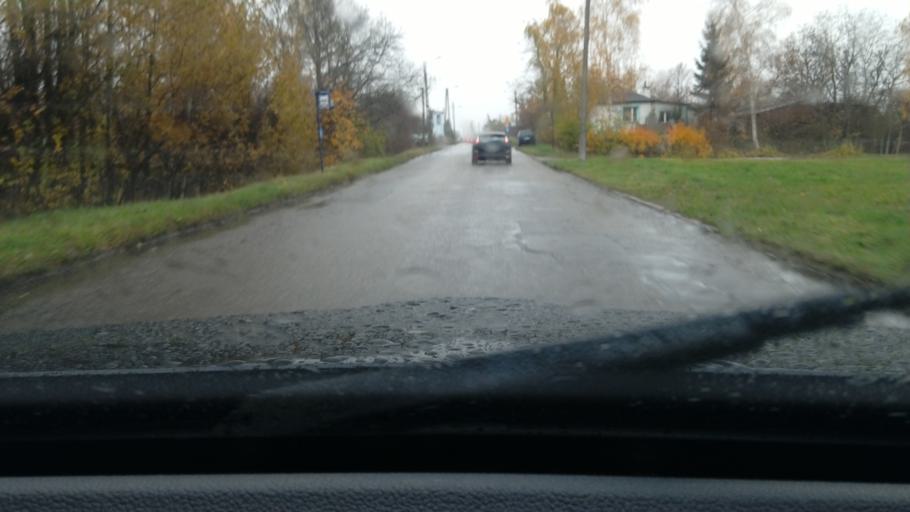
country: PL
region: Lodz Voivodeship
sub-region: Skierniewice
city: Skierniewice
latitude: 51.9451
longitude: 20.1499
